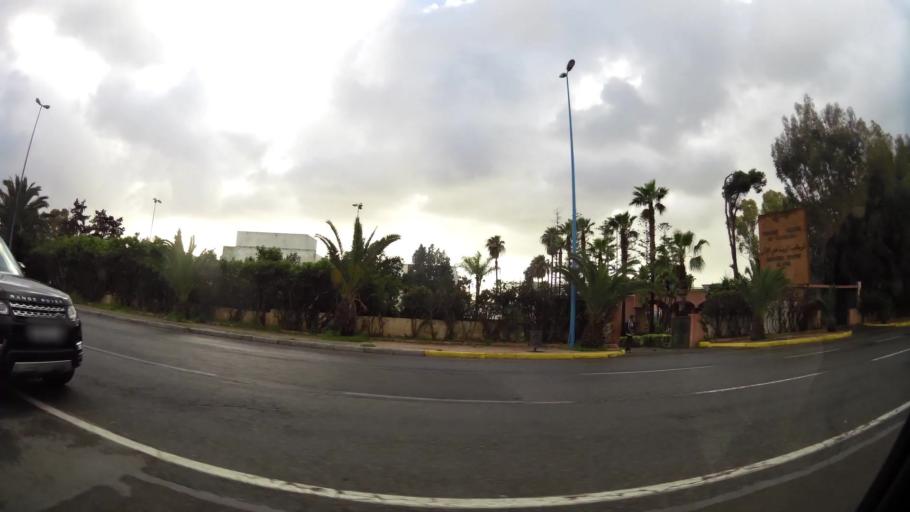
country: MA
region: Grand Casablanca
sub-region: Casablanca
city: Casablanca
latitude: 33.5566
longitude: -7.6503
